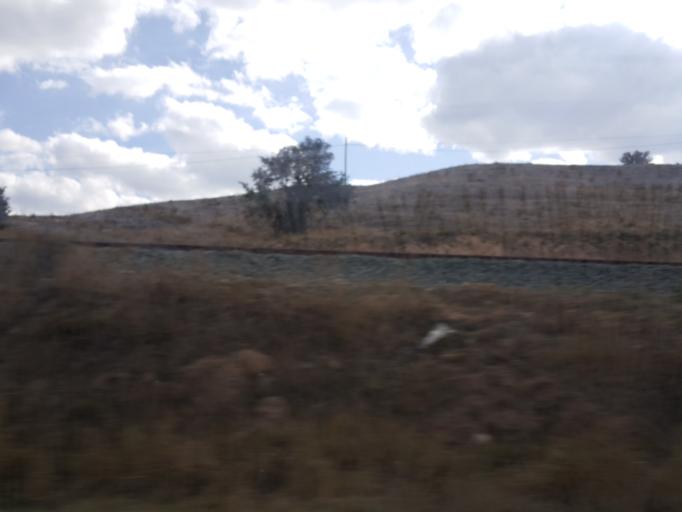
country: TR
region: Tokat
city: Yesilyurt
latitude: 40.0154
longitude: 36.2418
